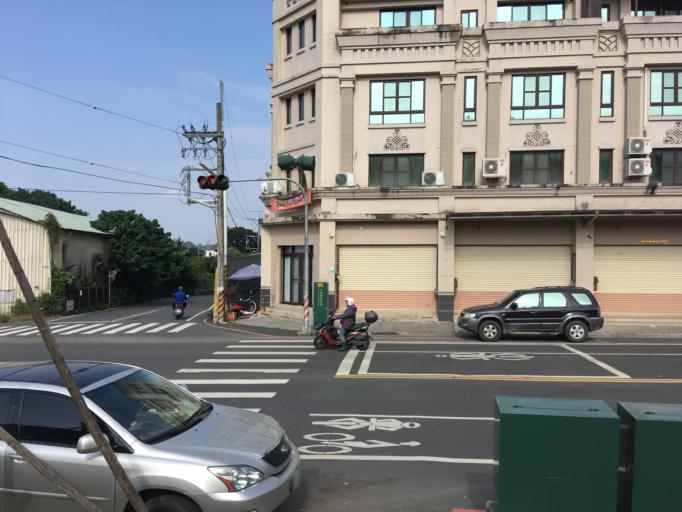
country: TW
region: Taiwan
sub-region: Chiayi
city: Jiayi Shi
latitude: 23.4942
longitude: 120.4989
